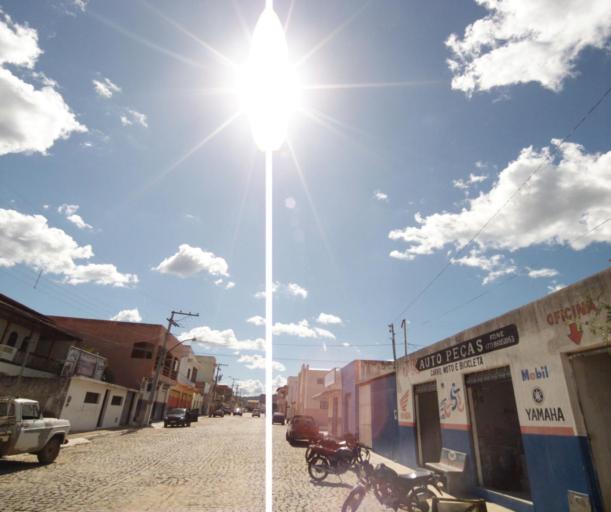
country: BR
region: Bahia
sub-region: Pocoes
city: Pocoes
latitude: -14.2411
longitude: -40.7706
